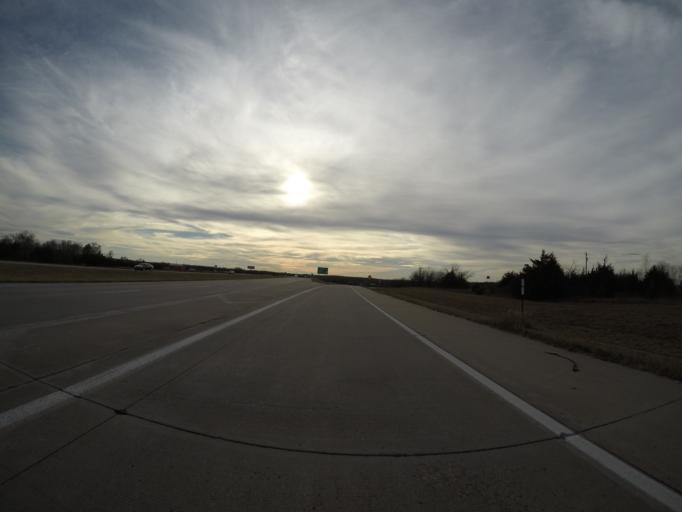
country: US
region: Kansas
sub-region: Franklin County
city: Ottawa
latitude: 38.4916
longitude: -95.4708
